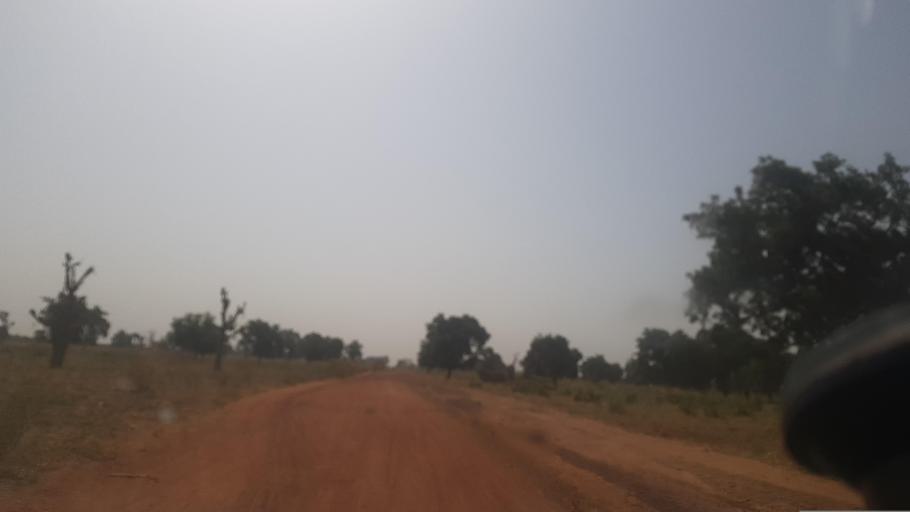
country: ML
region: Segou
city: Baroueli
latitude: 13.0024
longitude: -6.4192
